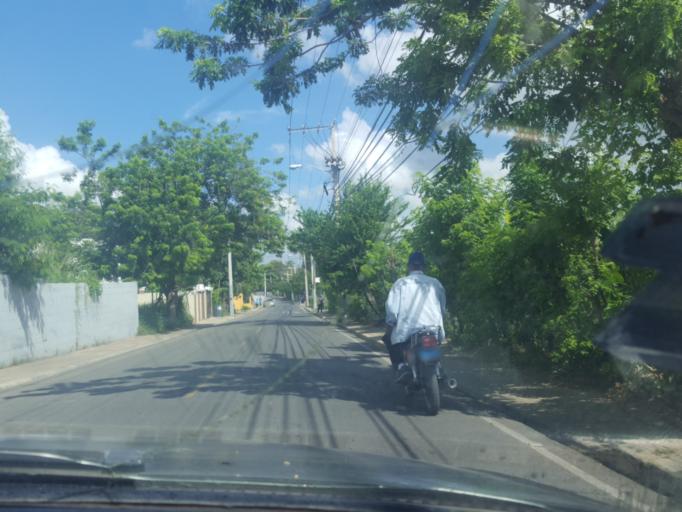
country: DO
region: Santiago
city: Santiago de los Caballeros
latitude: 19.4859
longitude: -70.6981
